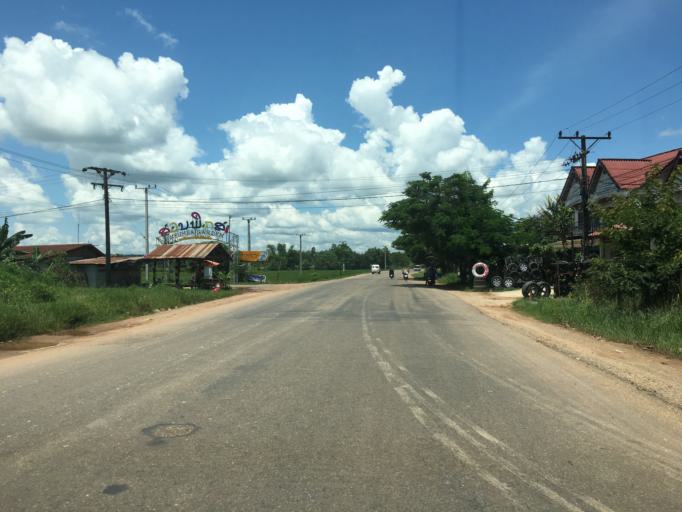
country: LA
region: Vientiane
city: Vientiane
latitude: 18.0929
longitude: 102.5130
